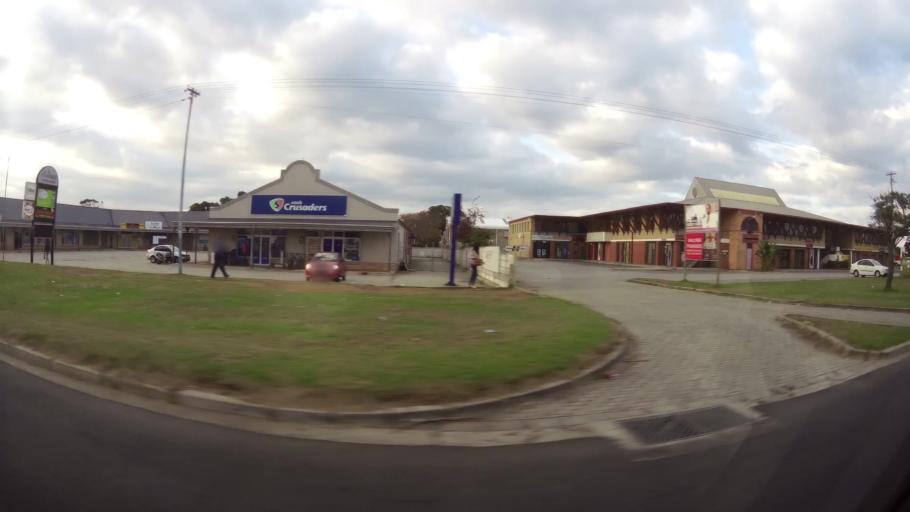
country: ZA
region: Eastern Cape
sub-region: Nelson Mandela Bay Metropolitan Municipality
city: Port Elizabeth
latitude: -33.9804
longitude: 25.5970
